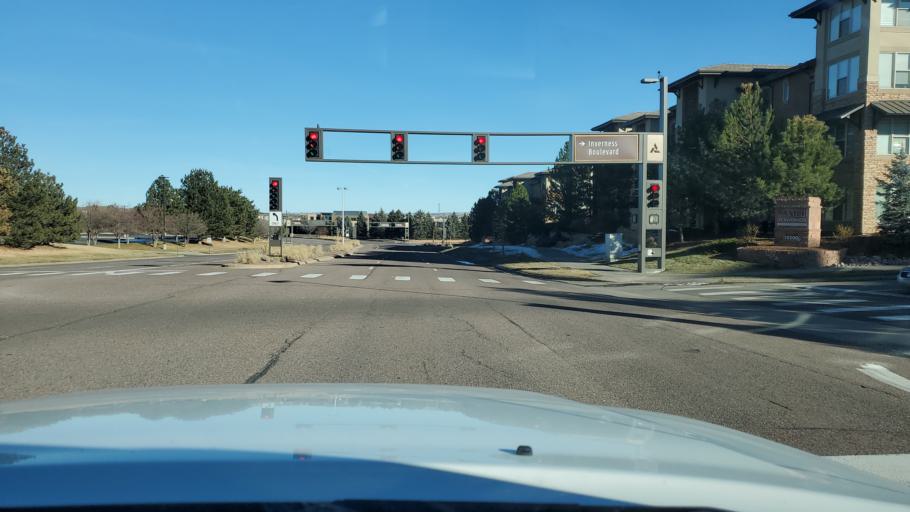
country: US
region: Colorado
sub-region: Arapahoe County
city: Centennial
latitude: 39.5807
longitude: -104.8706
